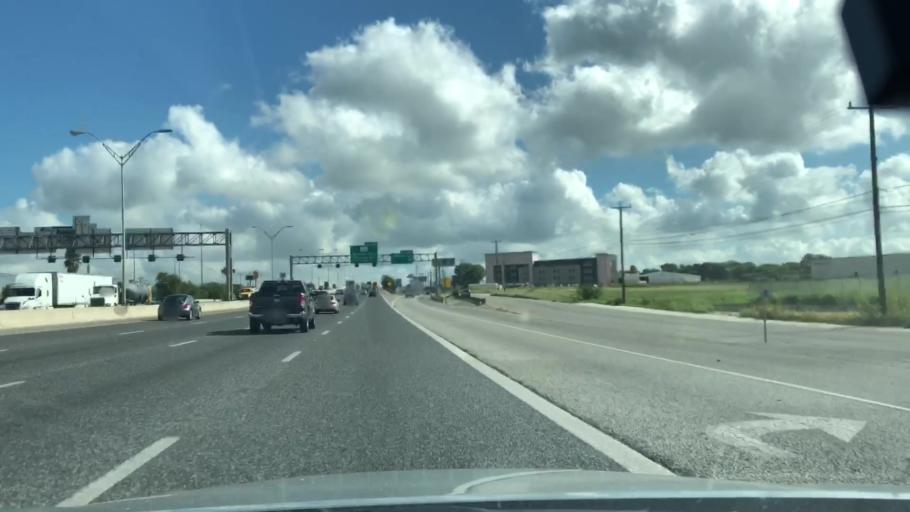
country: US
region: Texas
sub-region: Bexar County
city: Windcrest
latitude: 29.5366
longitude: -98.3848
